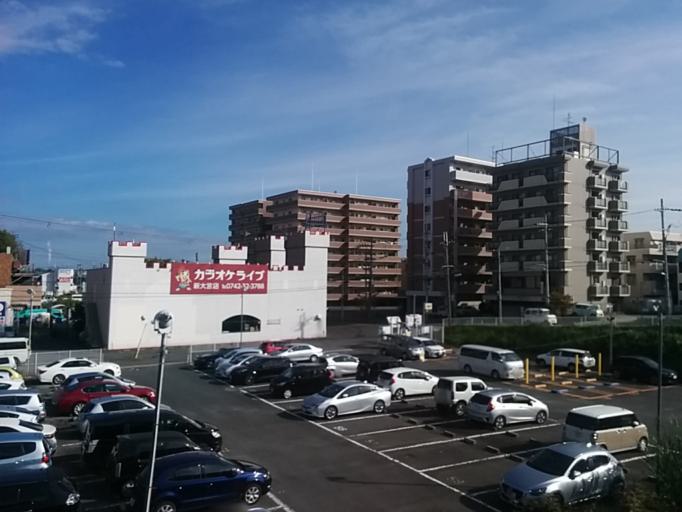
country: JP
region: Nara
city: Nara-shi
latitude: 34.6862
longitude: 135.8054
